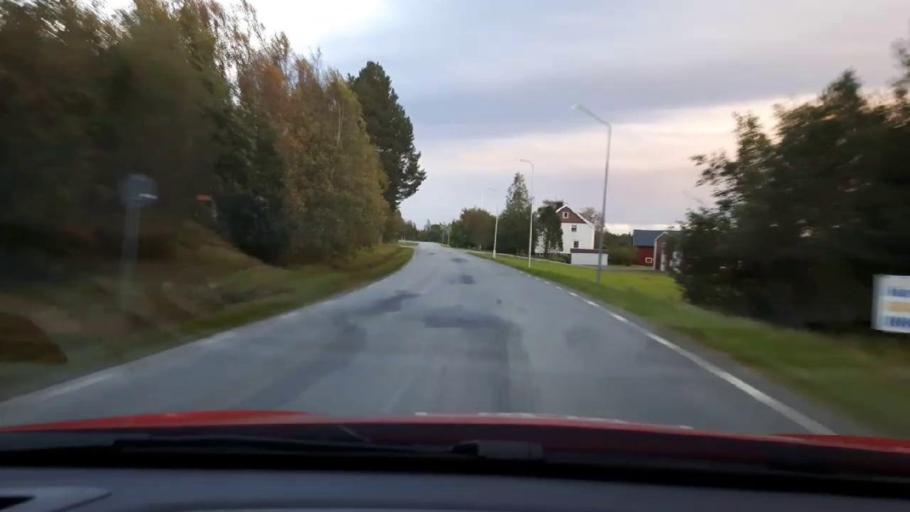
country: SE
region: Jaemtland
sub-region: Bergs Kommun
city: Hoverberg
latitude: 63.0247
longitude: 14.4751
